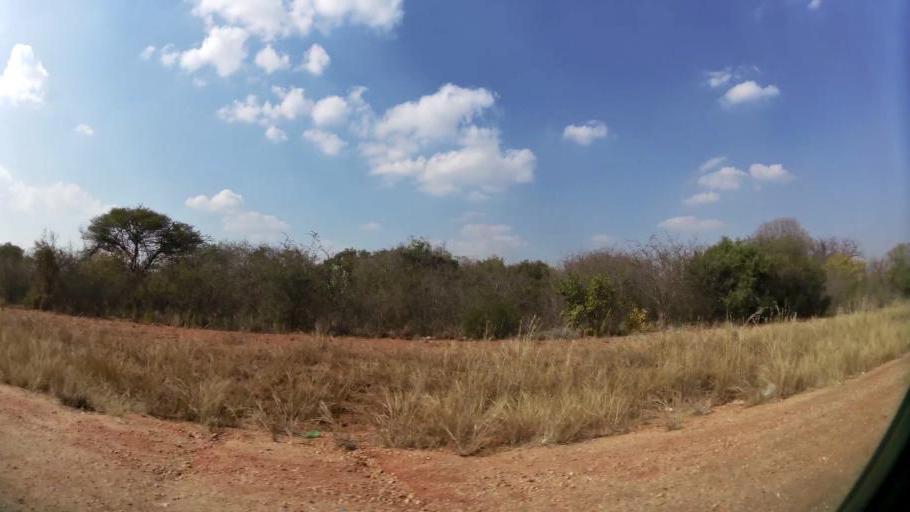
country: ZA
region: North-West
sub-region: Bojanala Platinum District Municipality
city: Mogwase
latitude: -25.4678
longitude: 27.0873
